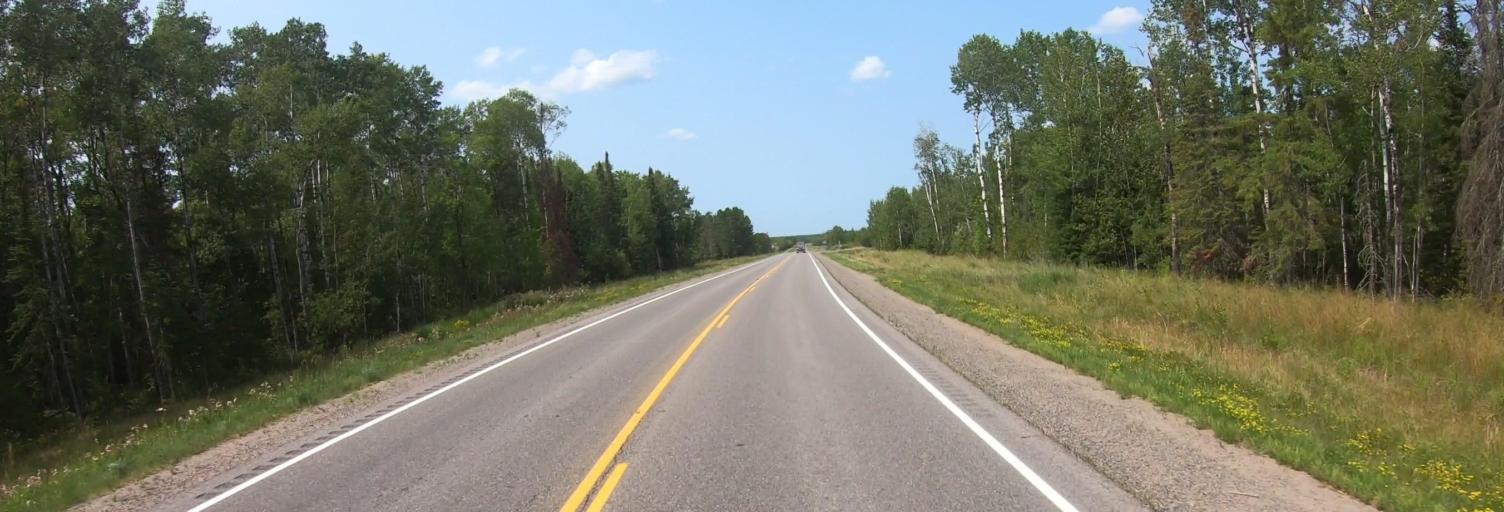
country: US
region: Minnesota
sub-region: Lake of the Woods County
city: Baudette
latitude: 48.6279
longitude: -94.1106
